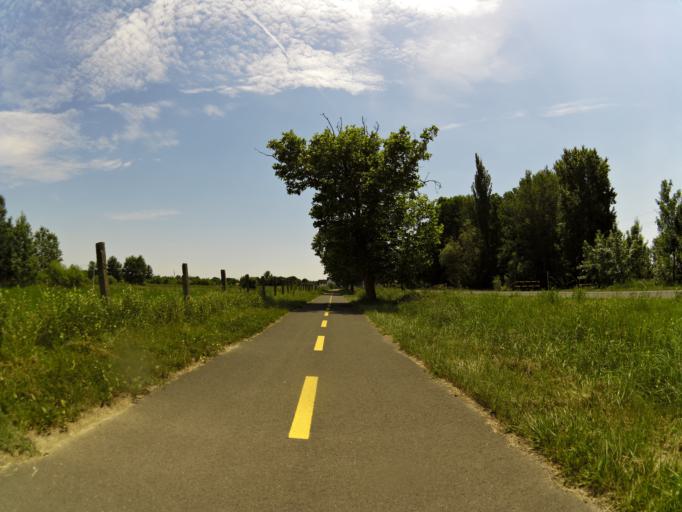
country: HU
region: Csongrad
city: Balastya
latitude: 46.4281
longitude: 20.0112
